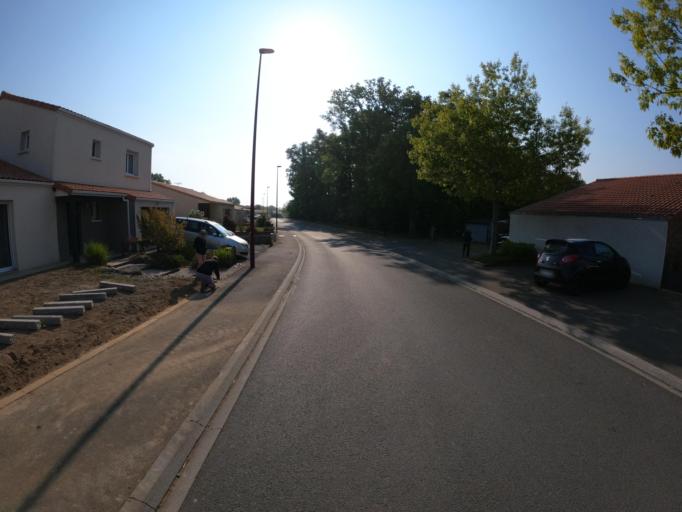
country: FR
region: Pays de la Loire
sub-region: Departement de Maine-et-Loire
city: La Seguiniere
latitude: 47.0664
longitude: -0.9494
